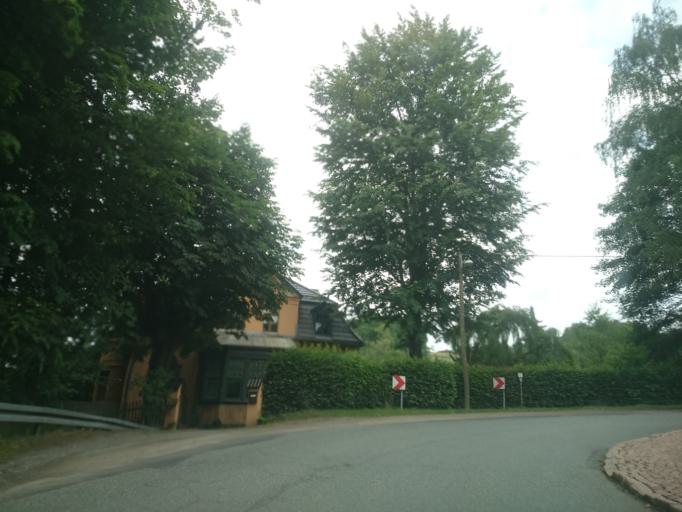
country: DE
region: Saxony
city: Borstendorf
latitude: 50.7751
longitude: 13.1647
